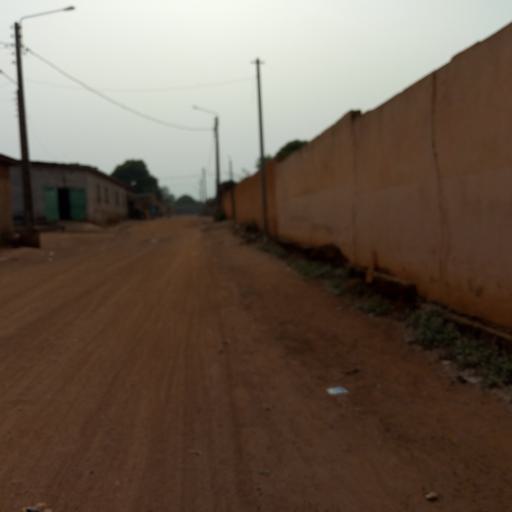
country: CI
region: Vallee du Bandama
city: Bouake
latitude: 7.7029
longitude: -5.0297
